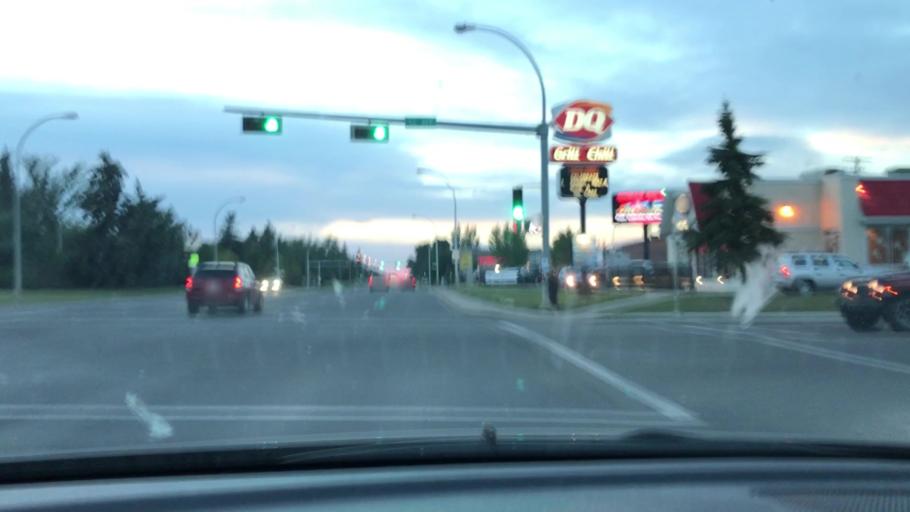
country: CA
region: Alberta
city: Edmonton
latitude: 53.5122
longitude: -113.4427
